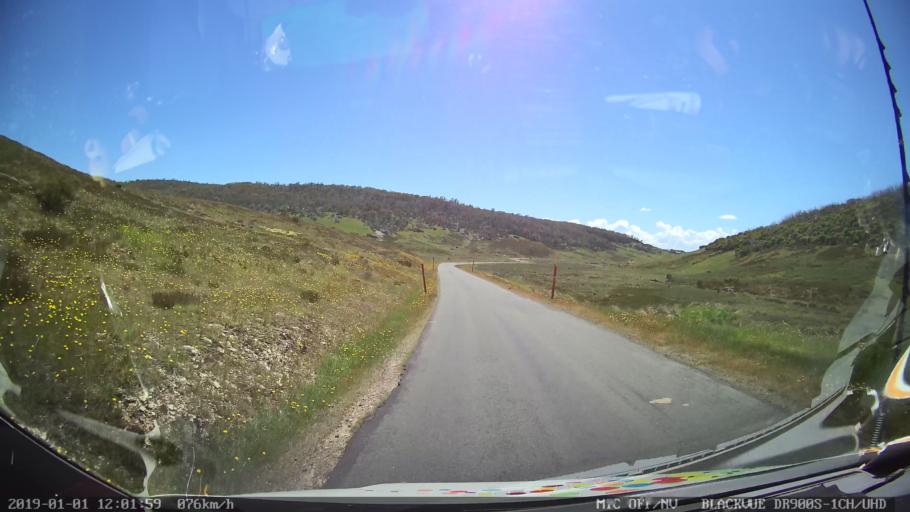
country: AU
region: New South Wales
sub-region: Snowy River
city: Jindabyne
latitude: -35.8760
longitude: 148.4732
